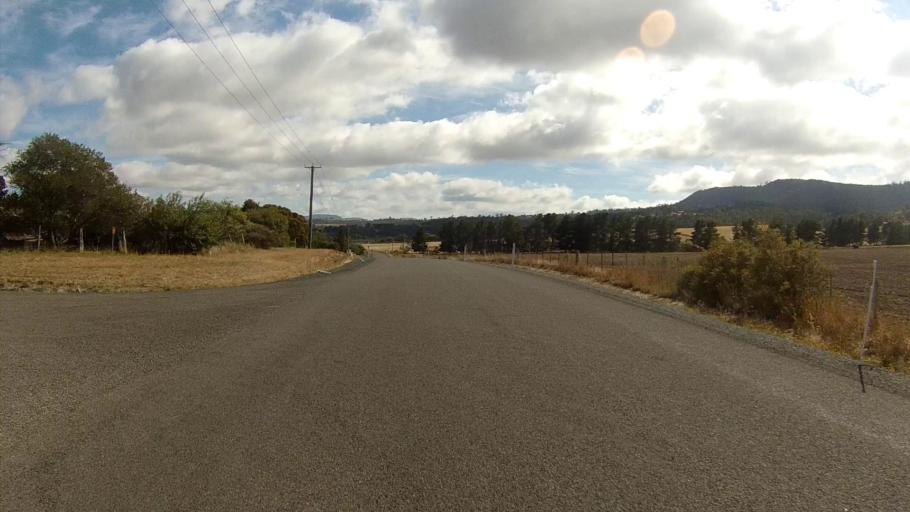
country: AU
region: Tasmania
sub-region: Brighton
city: Old Beach
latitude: -42.7652
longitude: 147.2996
